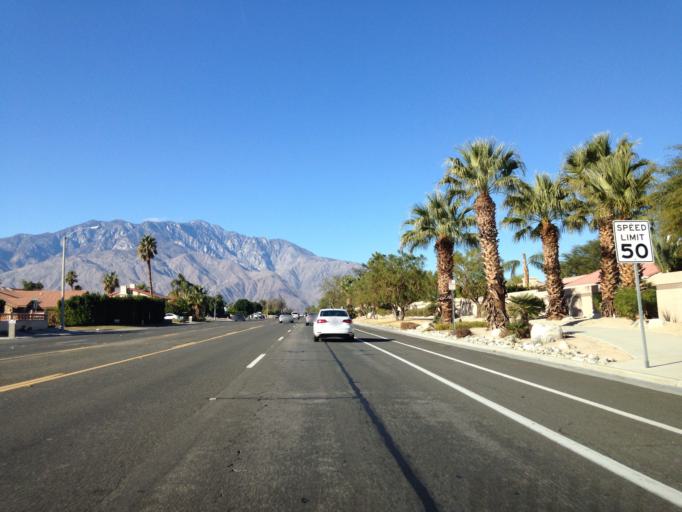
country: US
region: California
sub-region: Riverside County
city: Cathedral City
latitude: 33.8450
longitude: -116.4687
